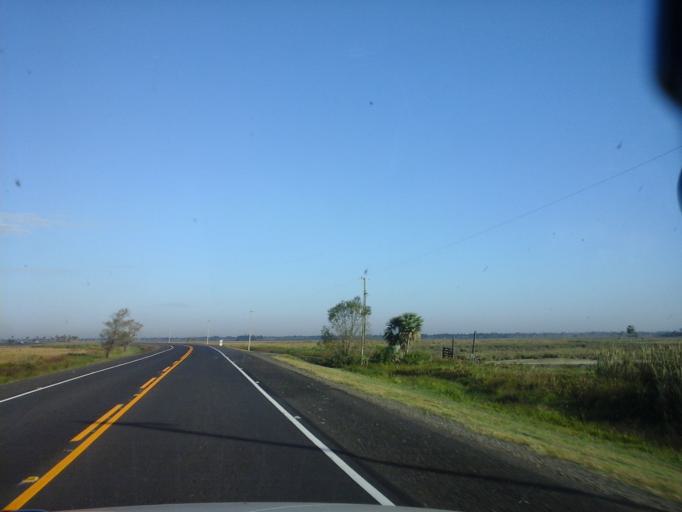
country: PY
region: Neembucu
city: Pilar
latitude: -26.8621
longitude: -57.8544
